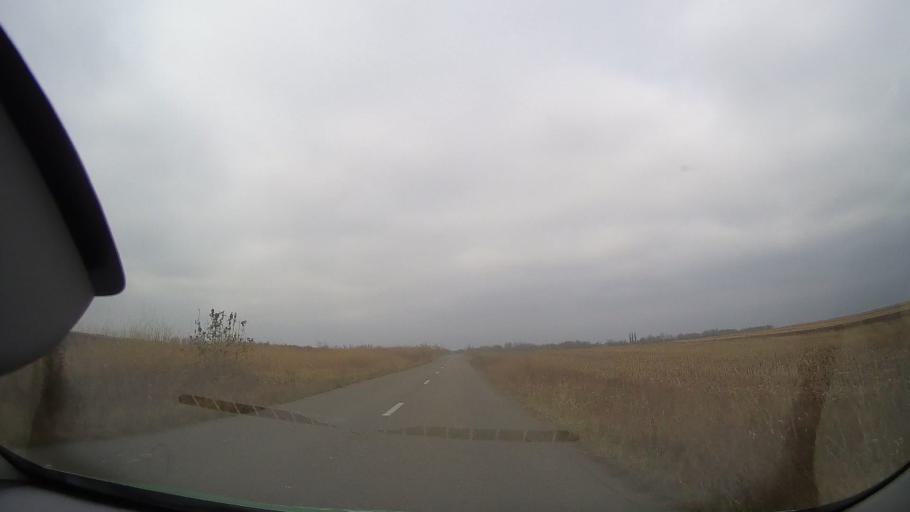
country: RO
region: Buzau
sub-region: Comuna Scutelnici
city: Scutelnici
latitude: 44.8686
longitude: 26.8908
